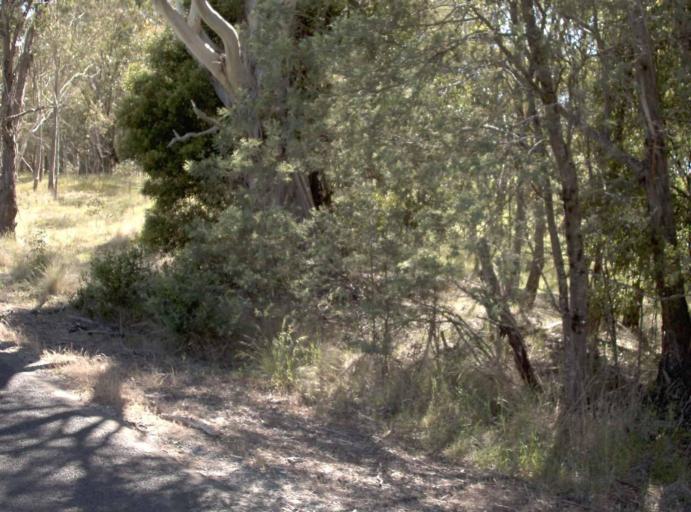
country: AU
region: New South Wales
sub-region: Bombala
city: Bombala
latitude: -37.0595
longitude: 148.8022
